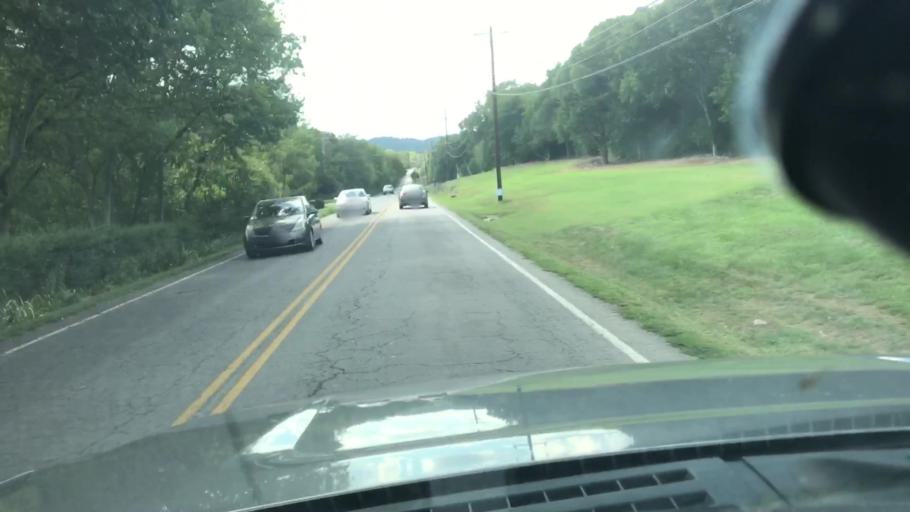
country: US
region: Tennessee
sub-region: Davidson County
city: Forest Hills
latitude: 36.0260
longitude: -86.8951
